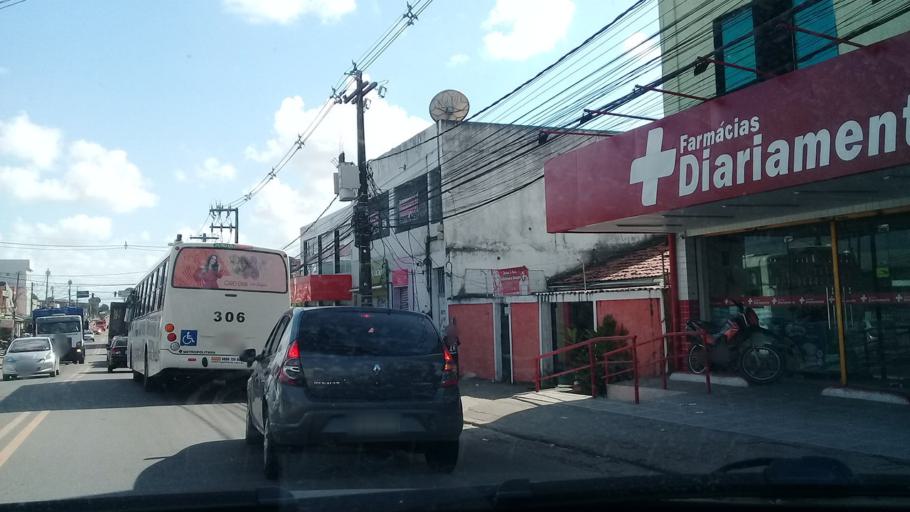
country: BR
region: Pernambuco
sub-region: Jaboatao Dos Guararapes
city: Jaboatao dos Guararapes
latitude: -8.1162
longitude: -34.9408
